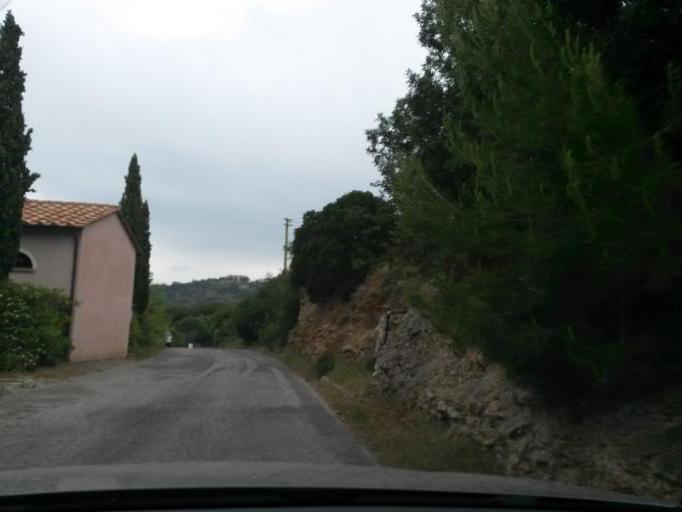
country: IT
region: Tuscany
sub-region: Provincia di Livorno
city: Capoliveri
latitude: 42.7366
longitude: 10.3721
